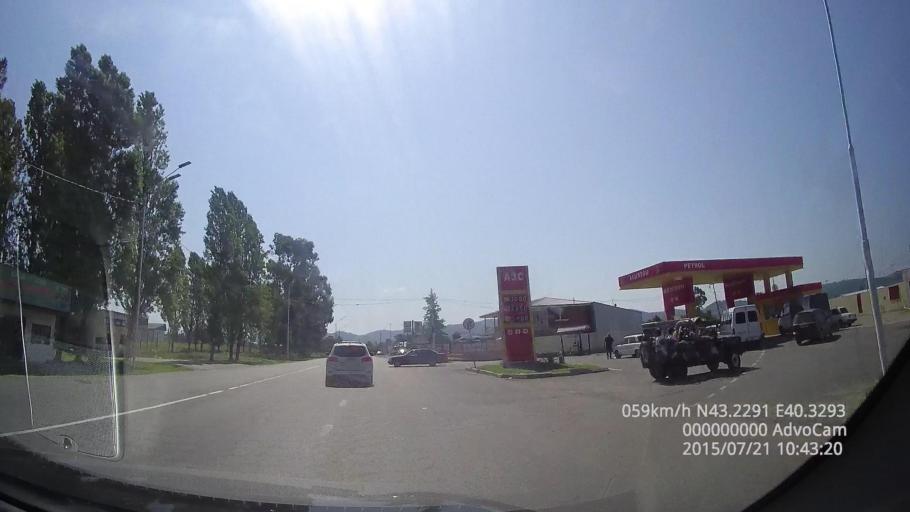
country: GE
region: Abkhazia
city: Bich'vinta
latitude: 43.2290
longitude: 40.3295
